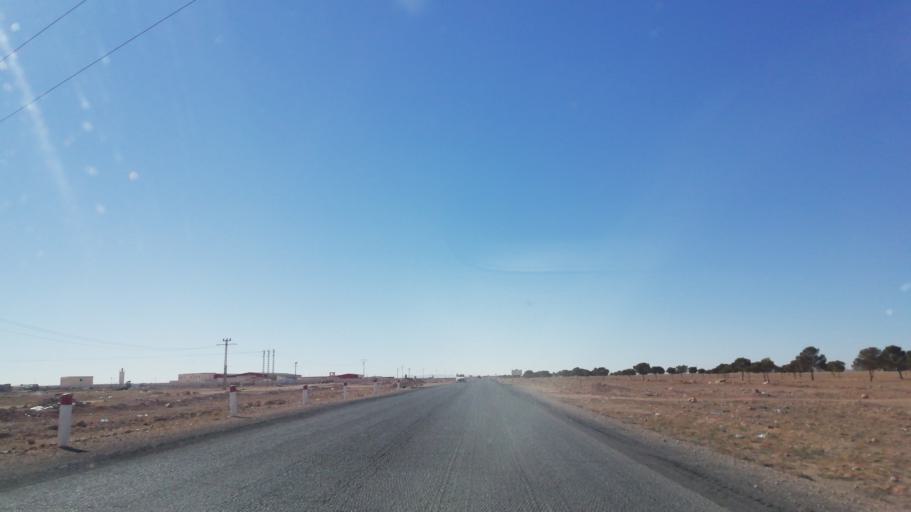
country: DZ
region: Saida
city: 'Ain el Hadjar
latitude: 34.0258
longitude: 0.0694
